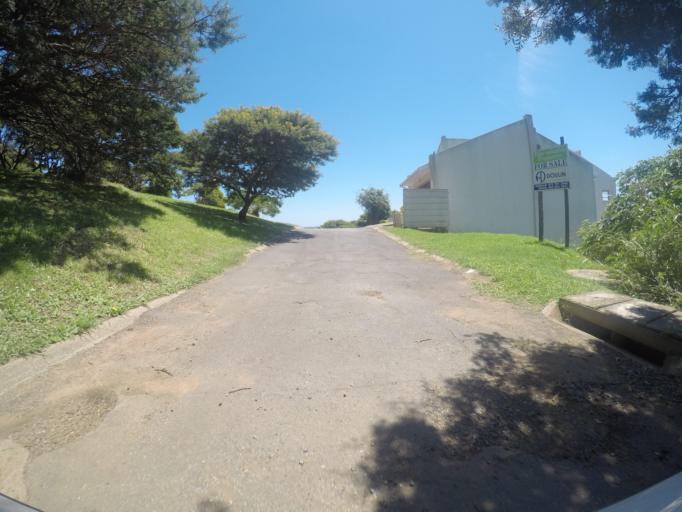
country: ZA
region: Eastern Cape
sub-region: Buffalo City Metropolitan Municipality
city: East London
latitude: -32.9317
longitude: 27.9939
